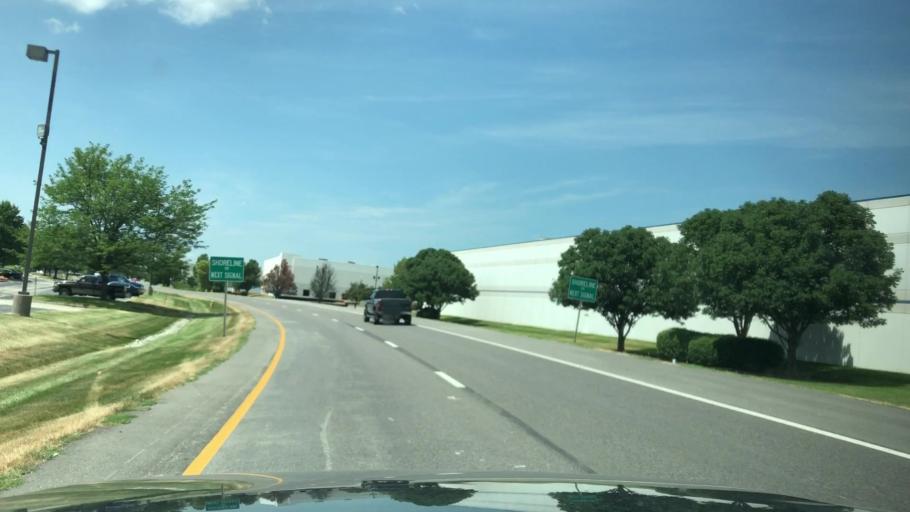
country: US
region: Missouri
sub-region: Saint Charles County
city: Saint Charles
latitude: 38.7702
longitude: -90.4574
